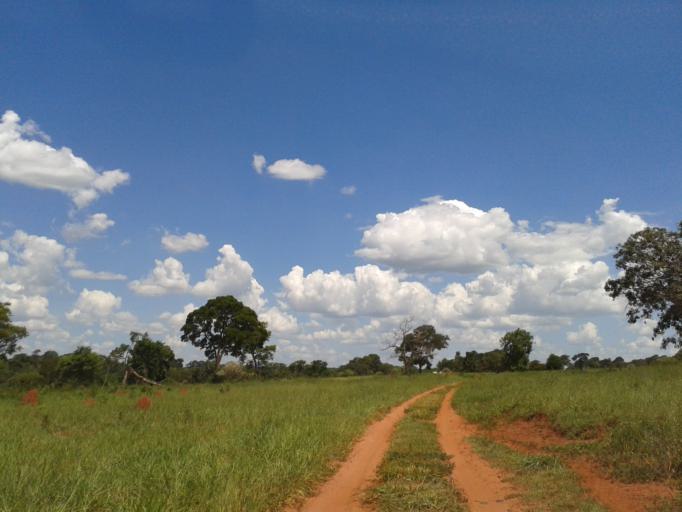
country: BR
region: Minas Gerais
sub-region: Santa Vitoria
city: Santa Vitoria
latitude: -19.1440
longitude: -50.5435
